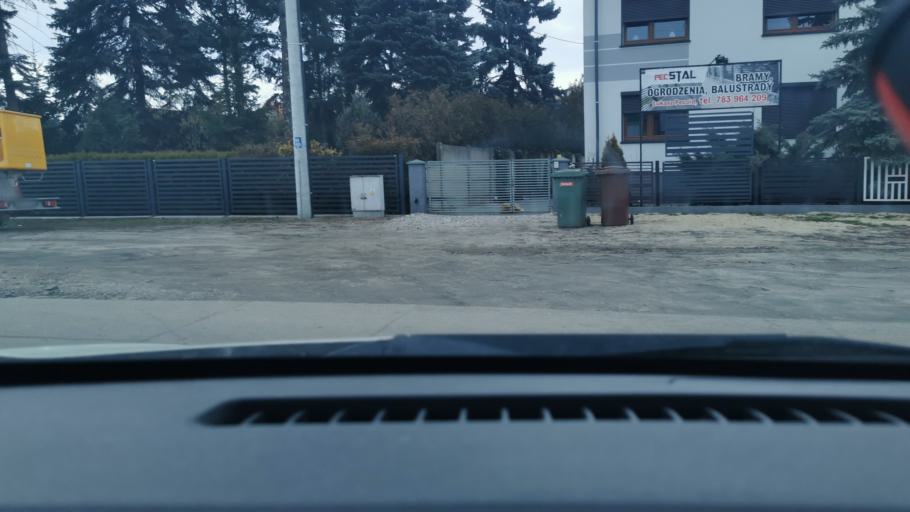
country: PL
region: Greater Poland Voivodeship
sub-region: Powiat ostrowski
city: Ostrow Wielkopolski
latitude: 51.6474
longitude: 17.8511
